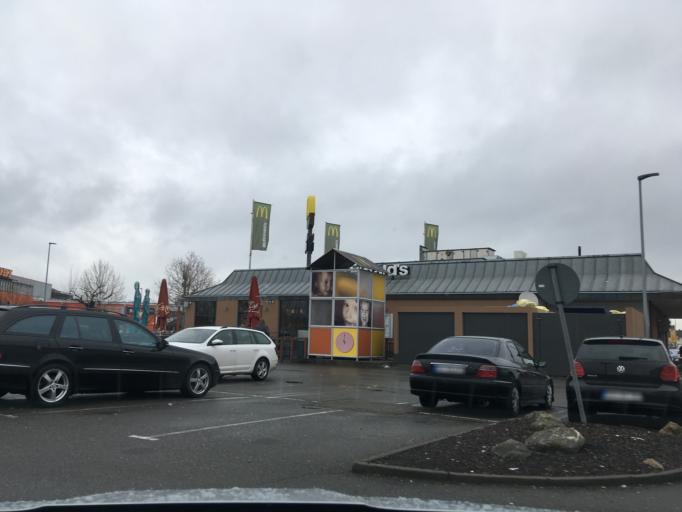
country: DE
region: Baden-Wuerttemberg
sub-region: Freiburg Region
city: Singen
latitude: 47.7527
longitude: 8.8529
